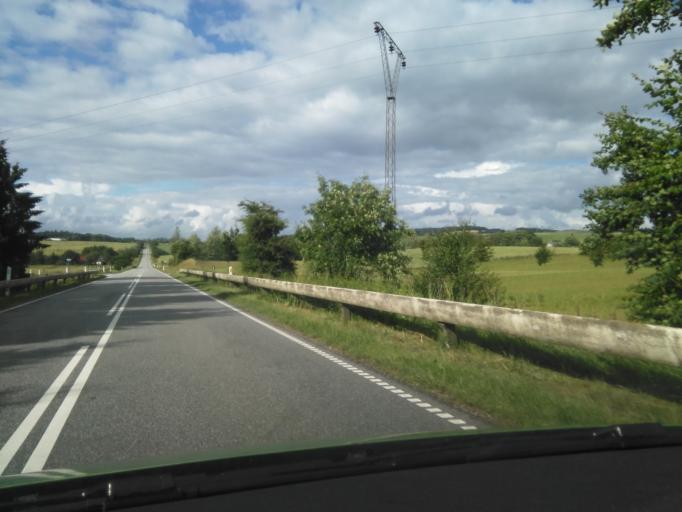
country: DK
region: Central Jutland
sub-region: Skanderborg Kommune
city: Ry
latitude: 55.9766
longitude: 9.7585
